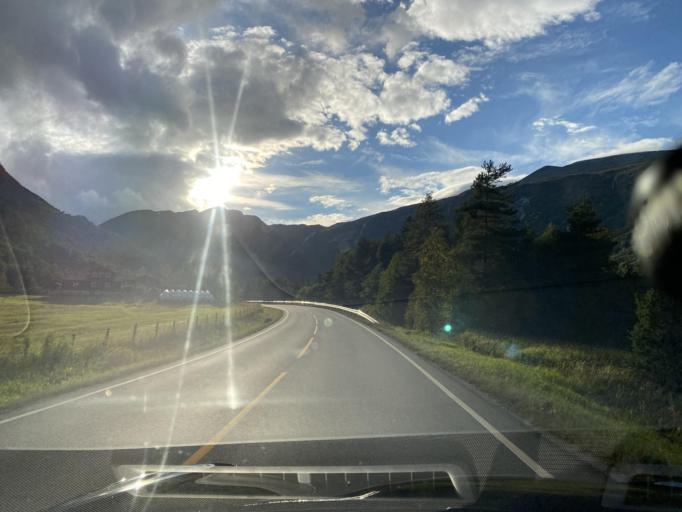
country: NO
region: Oppland
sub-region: Lom
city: Fossbergom
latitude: 61.8115
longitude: 8.4908
